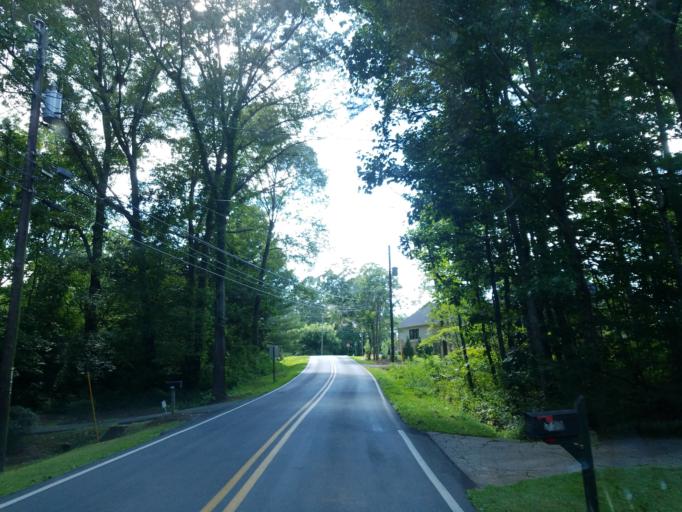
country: US
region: Georgia
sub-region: Pickens County
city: Jasper
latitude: 34.4601
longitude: -84.4273
